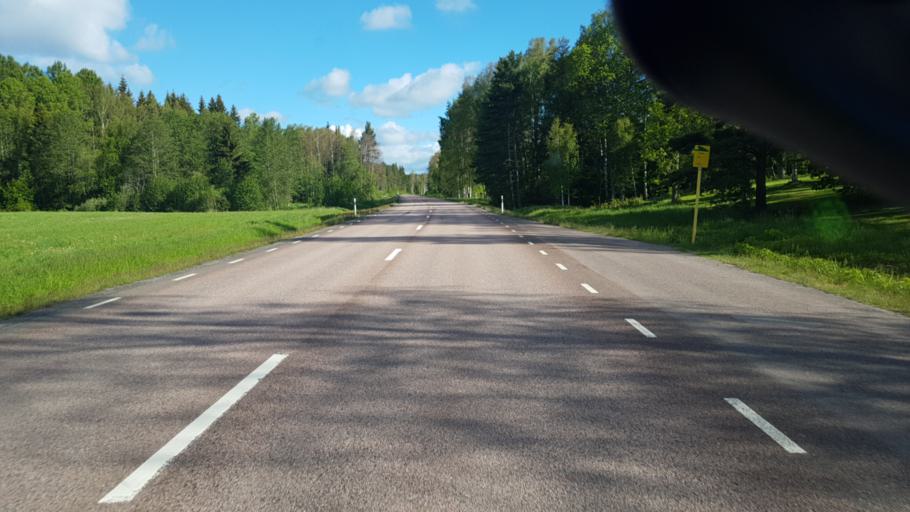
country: SE
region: Vaermland
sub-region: Arvika Kommun
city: Arvika
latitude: 59.6151
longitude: 12.6192
